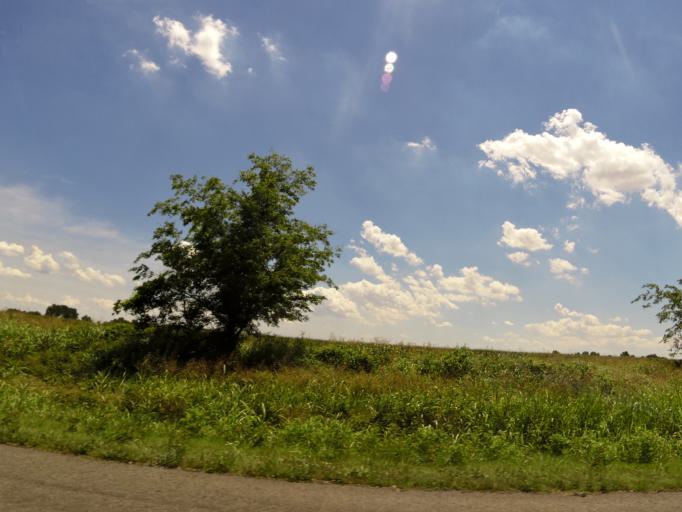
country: US
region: Missouri
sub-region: Pemiscot County
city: Caruthersville
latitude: 36.1398
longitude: -89.6374
